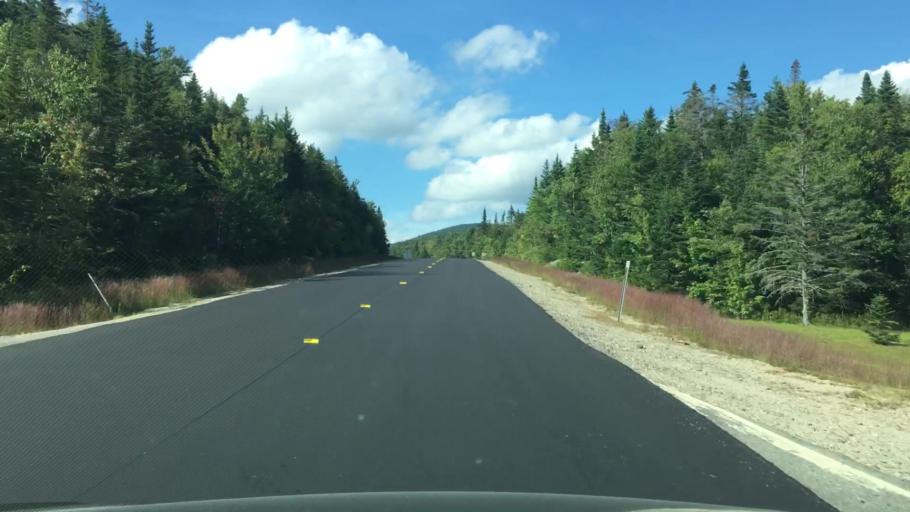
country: US
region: New Hampshire
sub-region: Grafton County
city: Woodstock
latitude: 44.0235
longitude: -71.4927
